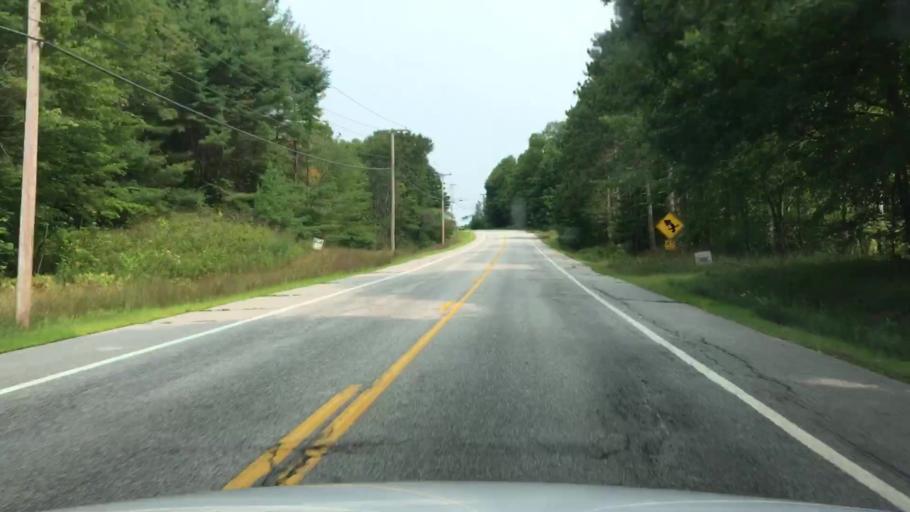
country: US
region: Maine
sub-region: Androscoggin County
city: Livermore Falls
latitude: 44.4206
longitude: -70.1446
